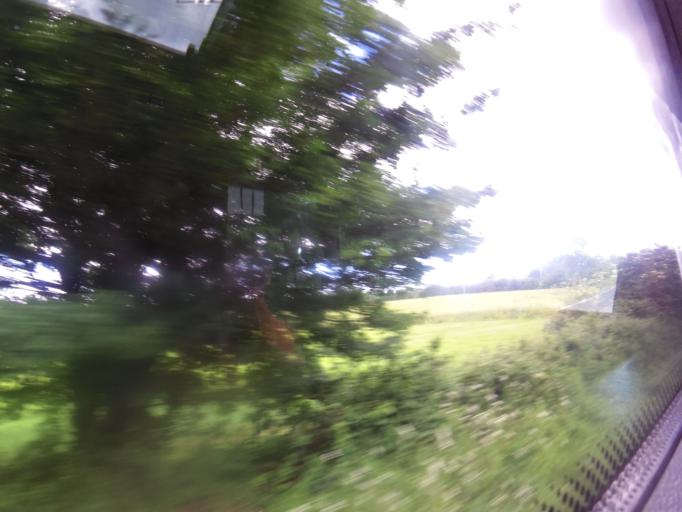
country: GB
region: England
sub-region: Norfolk
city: Cromer
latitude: 52.8896
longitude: 1.2977
